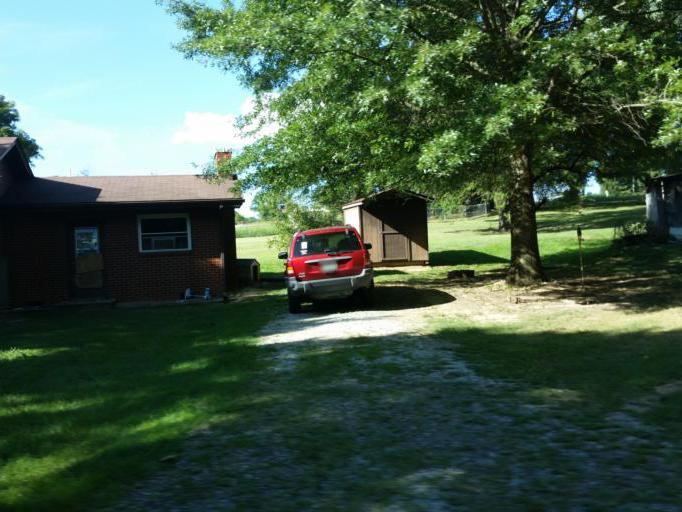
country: US
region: Tennessee
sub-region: Greene County
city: Tusculum
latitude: 36.1910
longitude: -82.7356
